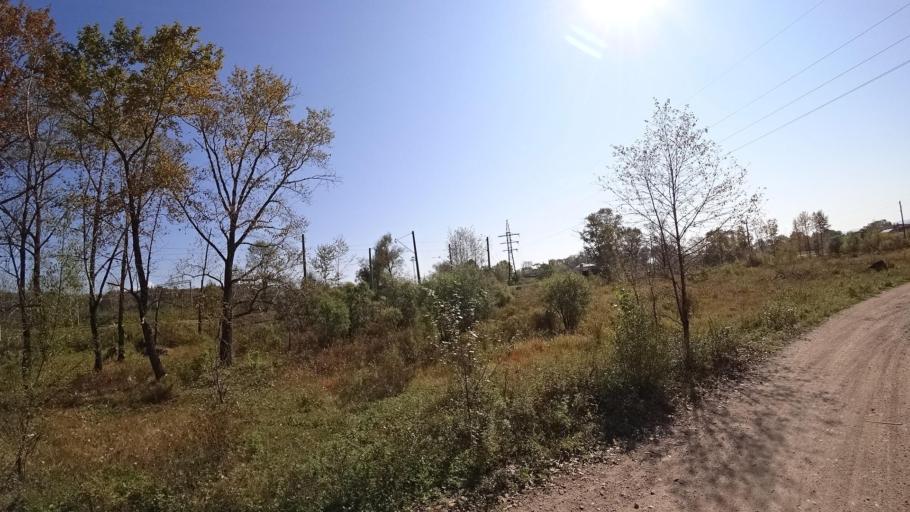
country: RU
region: Jewish Autonomous Oblast
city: Bira
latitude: 49.0016
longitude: 132.4509
